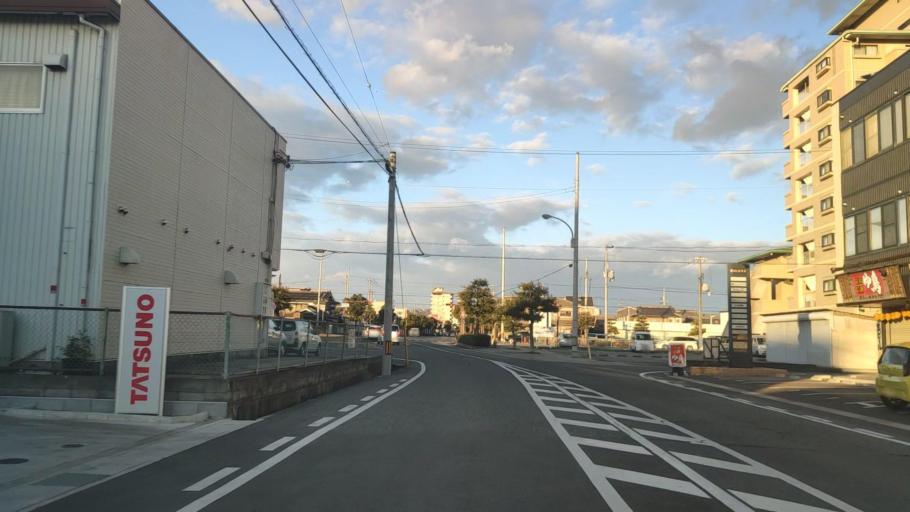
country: JP
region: Hyogo
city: Himeji
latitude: 34.8138
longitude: 134.6892
